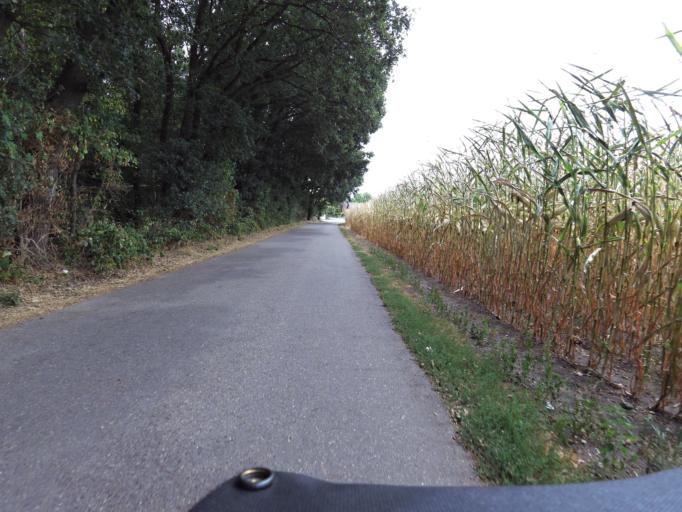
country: NL
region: Limburg
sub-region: Gemeente Bergen
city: Wellerlooi
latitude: 51.5769
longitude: 6.1635
